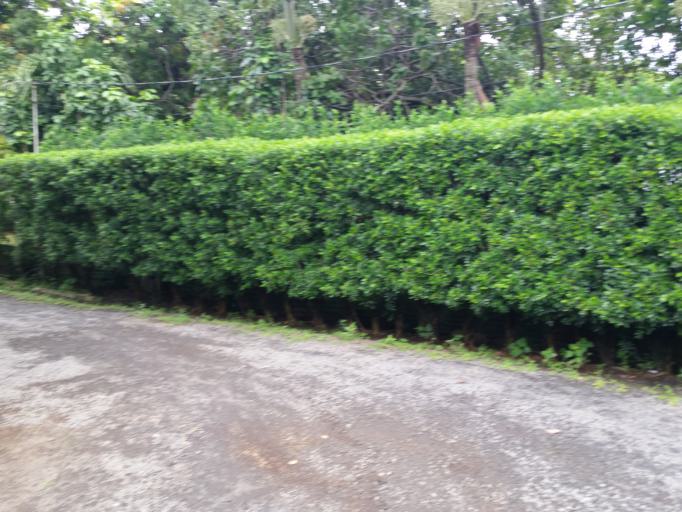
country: NI
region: Managua
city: Managua
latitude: 12.0867
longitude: -86.2301
